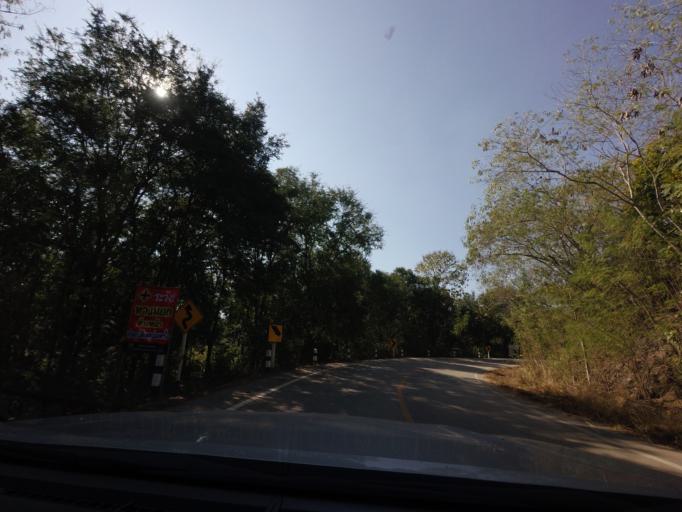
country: TH
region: Lampang
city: Chae Hom
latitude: 18.5942
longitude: 99.6277
